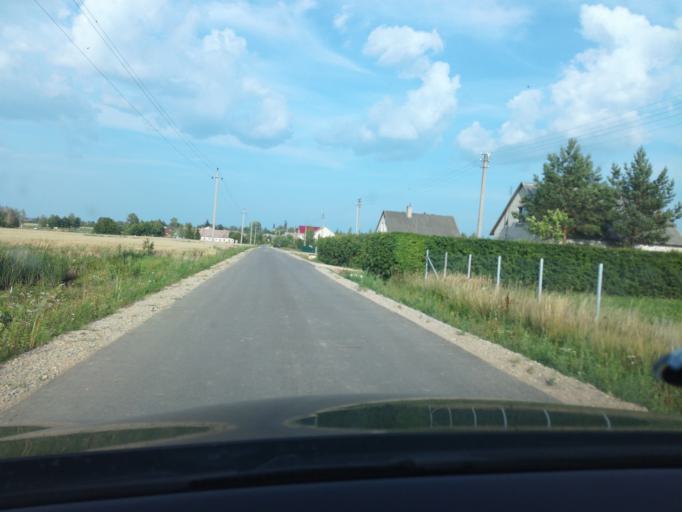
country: LT
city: Simnas
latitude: 54.3851
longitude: 23.6788
